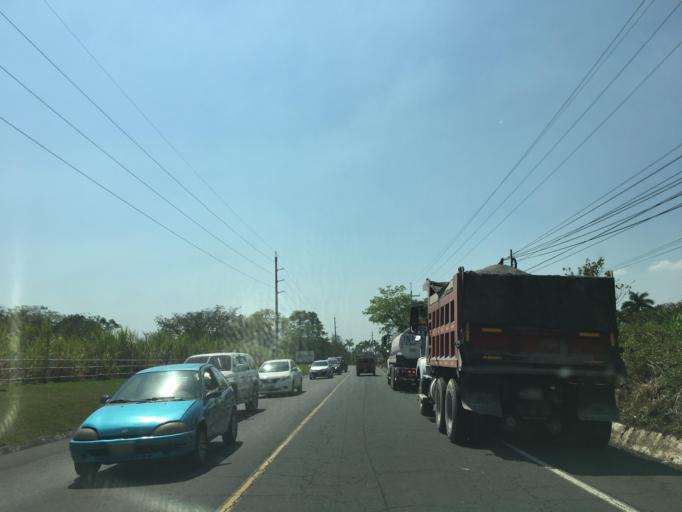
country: GT
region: Escuintla
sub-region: Municipio de Escuintla
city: Escuintla
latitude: 14.3283
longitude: -90.7969
